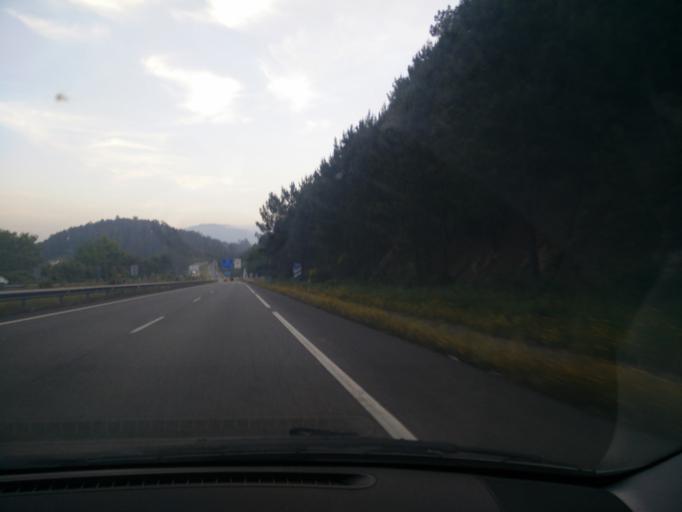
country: ES
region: Galicia
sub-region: Provincia de Pontevedra
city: Porrino
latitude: 42.1674
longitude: -8.5932
